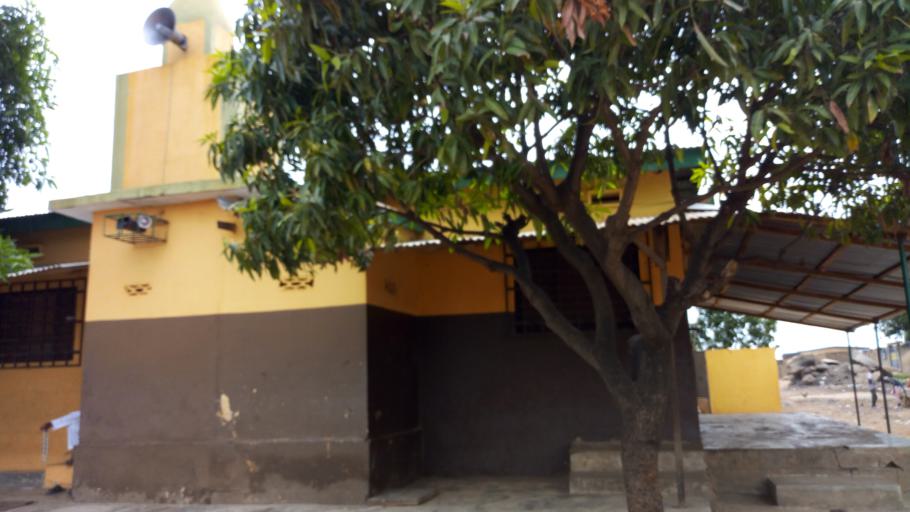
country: CI
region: Vallee du Bandama
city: Bouake
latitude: 7.7263
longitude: -5.0225
